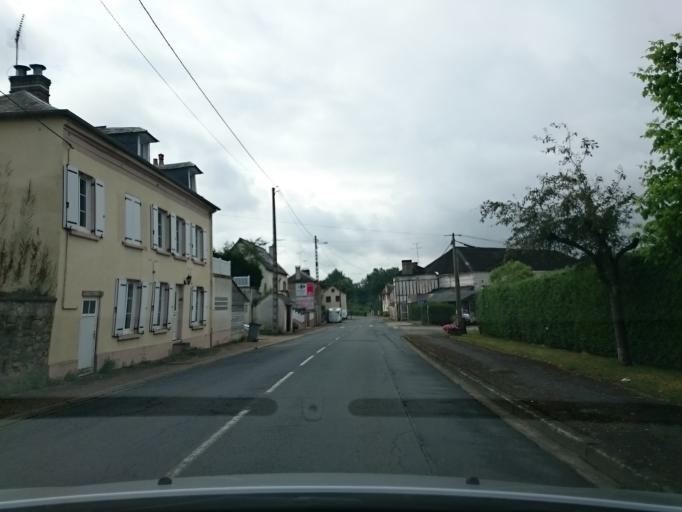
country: FR
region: Lower Normandy
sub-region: Departement du Calvados
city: Beuvillers
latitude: 49.1061
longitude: 0.2928
